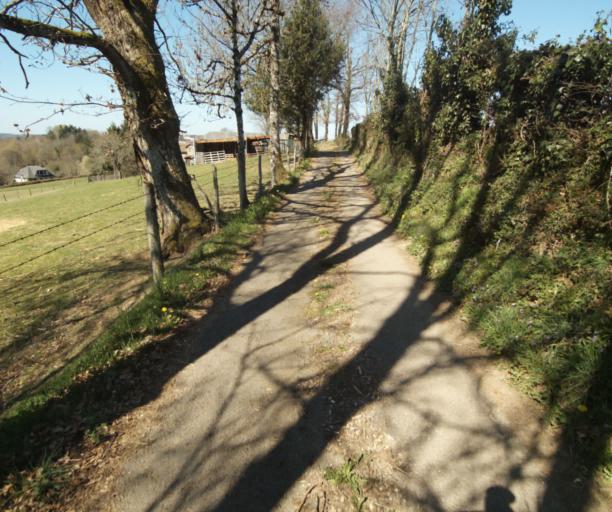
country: FR
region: Limousin
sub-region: Departement de la Correze
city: Saint-Mexant
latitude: 45.3087
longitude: 1.6419
